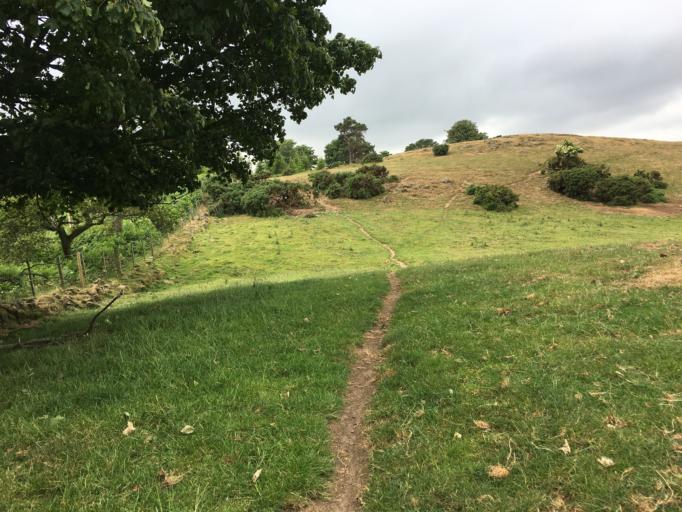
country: GB
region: England
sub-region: Northumberland
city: Belford
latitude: 55.6041
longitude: -1.8562
